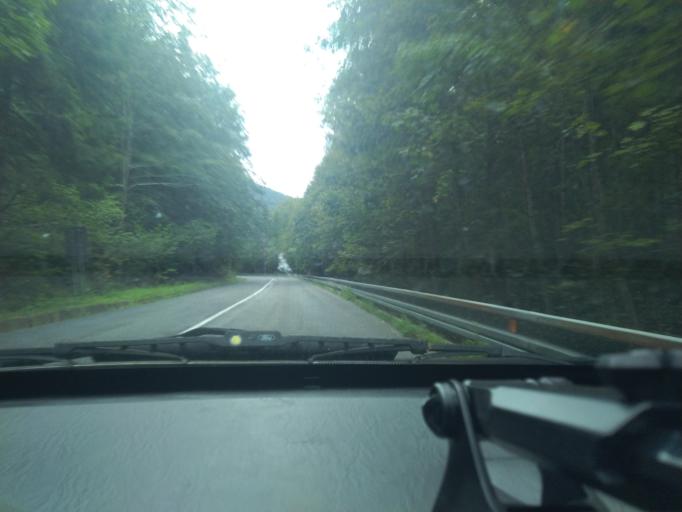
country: SK
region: Banskobystricky
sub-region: Okres Banska Bystrica
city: Banska Bystrica
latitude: 48.8224
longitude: 19.0294
